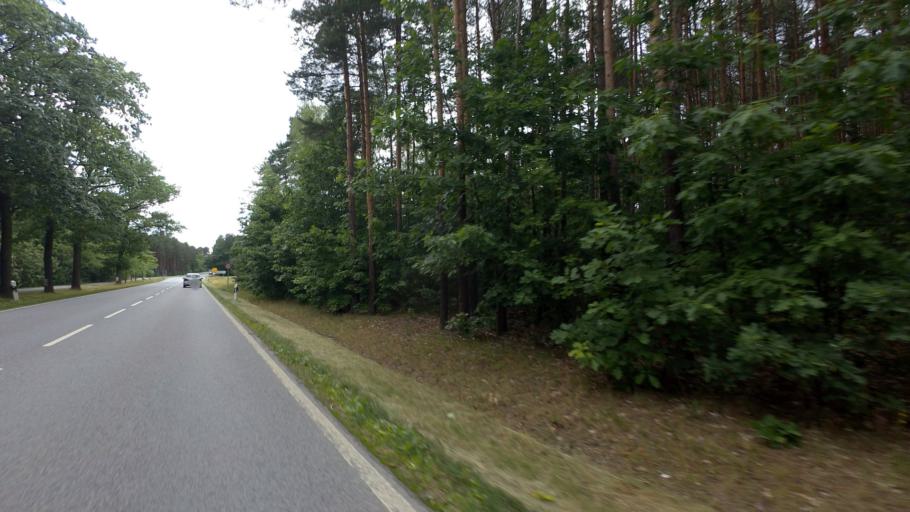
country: DE
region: Saxony
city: Ossling
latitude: 51.3665
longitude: 14.1797
